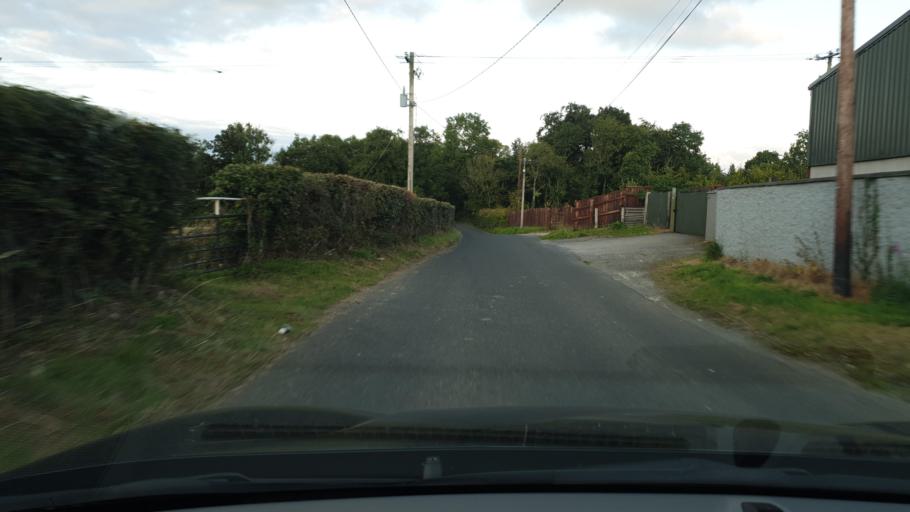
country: IE
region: Leinster
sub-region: Kildare
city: Kill
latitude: 53.2535
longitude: -6.5373
